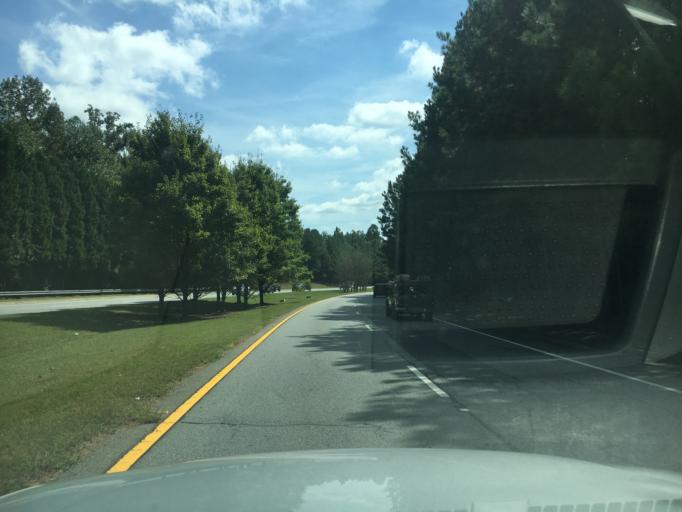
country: US
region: Georgia
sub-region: Gwinnett County
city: Duluth
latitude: 34.0093
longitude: -84.1010
